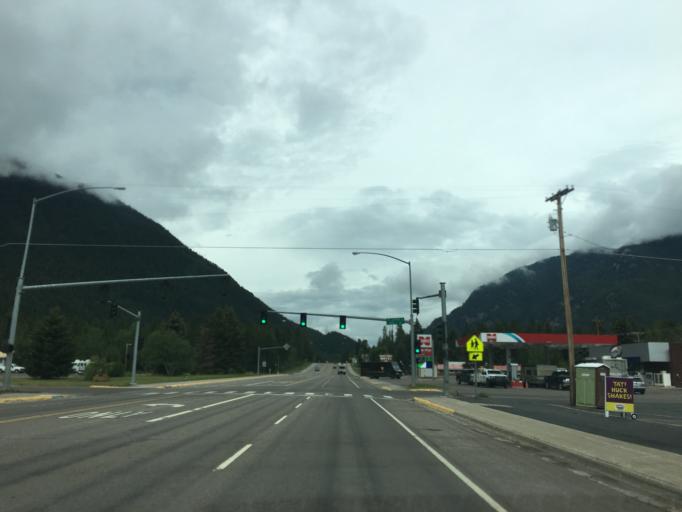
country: US
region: Montana
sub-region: Flathead County
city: Columbia Falls
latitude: 48.3857
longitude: -114.0632
